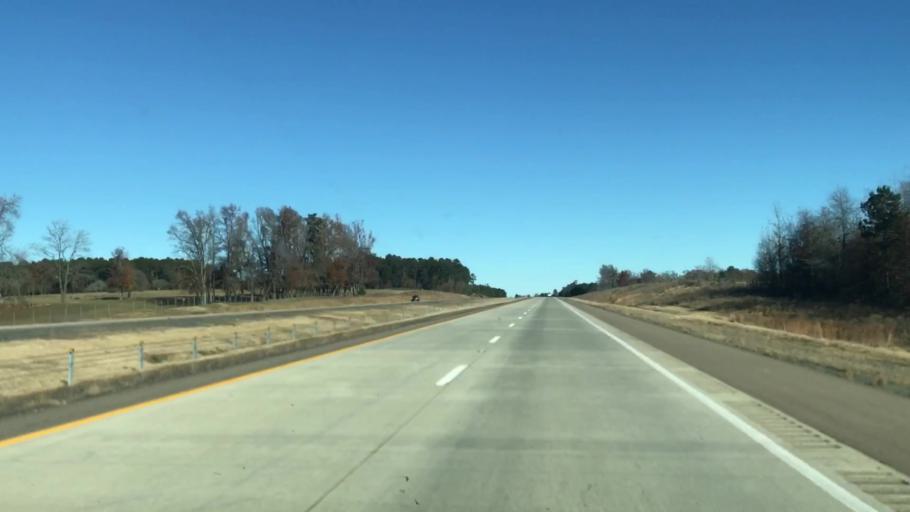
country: US
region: Louisiana
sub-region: Caddo Parish
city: Vivian
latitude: 33.0385
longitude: -93.9007
